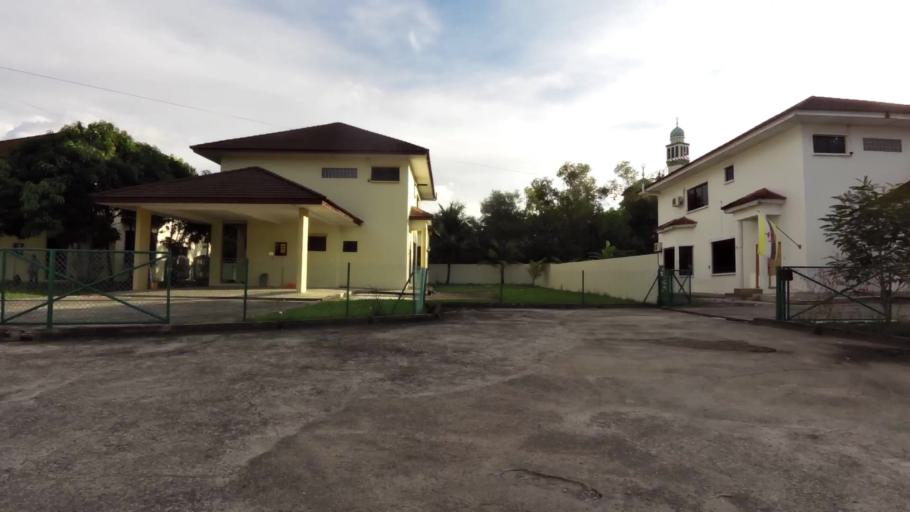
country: BN
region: Brunei and Muara
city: Bandar Seri Begawan
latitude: 4.9761
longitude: 114.9818
